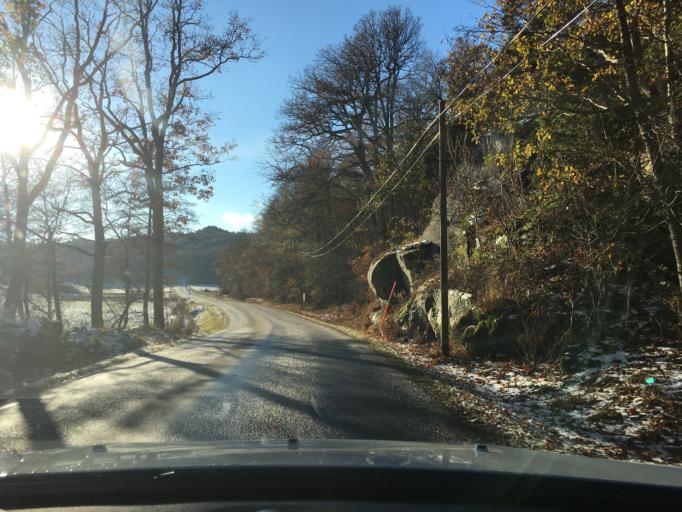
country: SE
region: Vaestra Goetaland
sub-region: Tjorns Kommun
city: Myggenas
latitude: 58.0558
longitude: 11.6769
